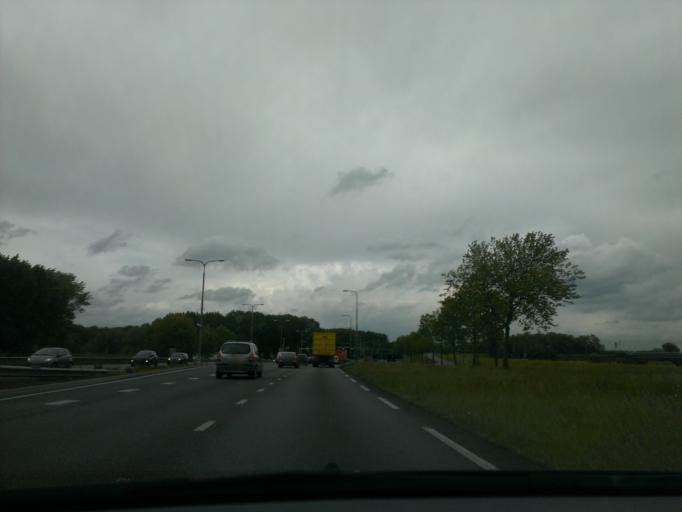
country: NL
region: Gelderland
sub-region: Gemeente Westervoort
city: Westervoort
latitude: 51.9683
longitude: 5.9529
